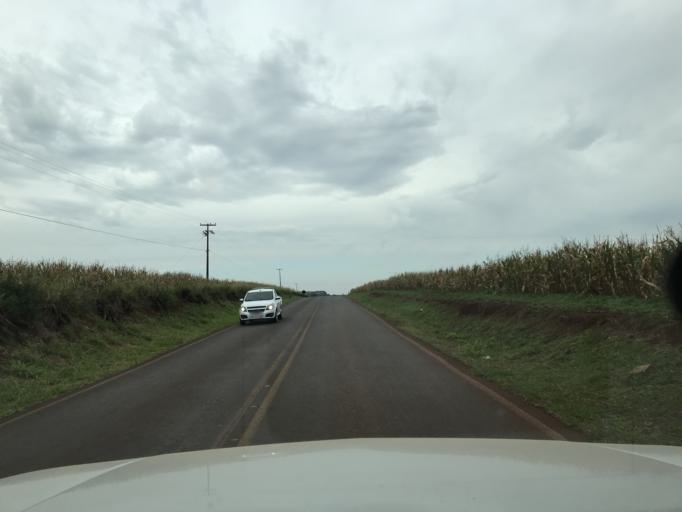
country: BR
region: Parana
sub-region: Marechal Candido Rondon
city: Marechal Candido Rondon
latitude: -24.4516
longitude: -53.9287
